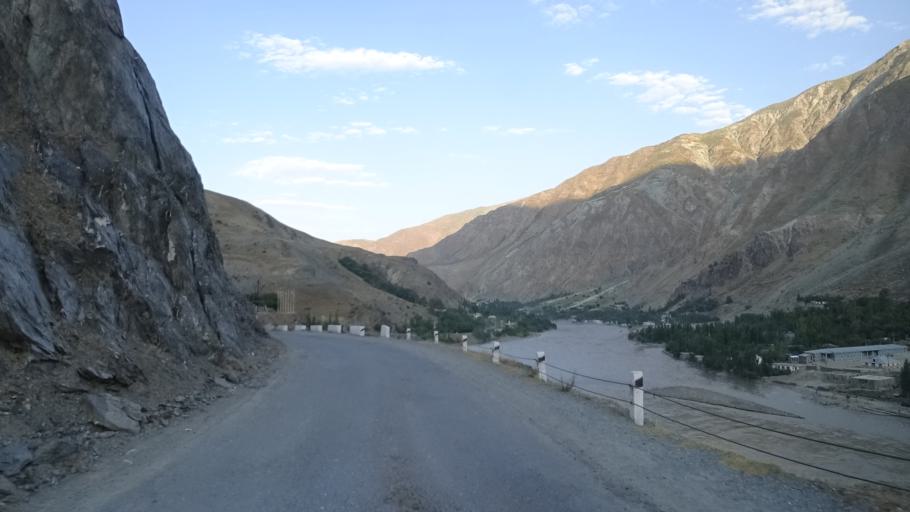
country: TJ
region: Gorno-Badakhshan
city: Qalaikhumb
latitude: 38.4502
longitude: 70.7942
